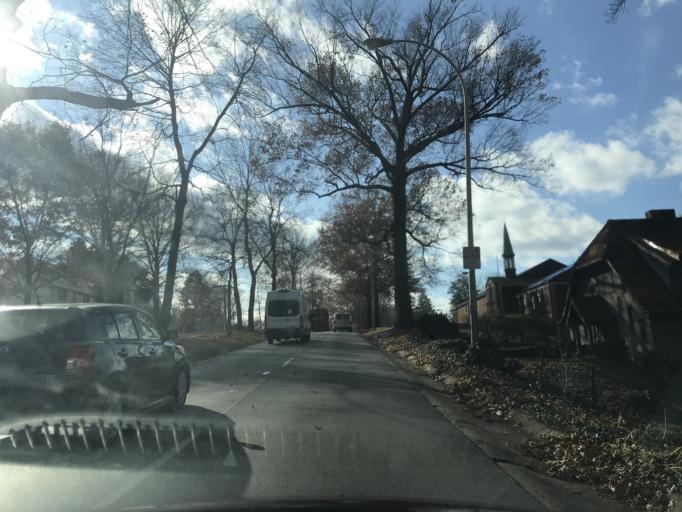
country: US
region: Kentucky
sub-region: Jefferson County
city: Audubon Park
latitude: 38.2275
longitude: -85.7186
